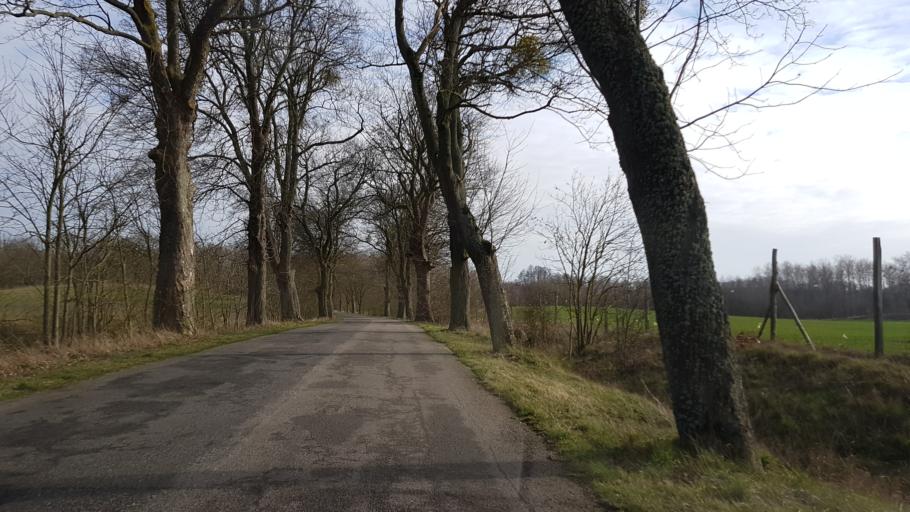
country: PL
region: West Pomeranian Voivodeship
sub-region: Powiat policki
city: Dobra
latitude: 53.5404
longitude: 14.3139
